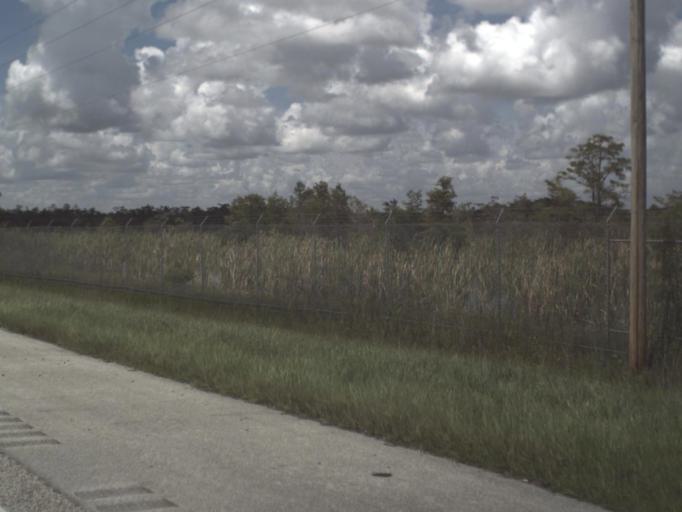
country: US
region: Florida
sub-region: Collier County
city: Immokalee
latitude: 26.1696
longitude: -81.0319
